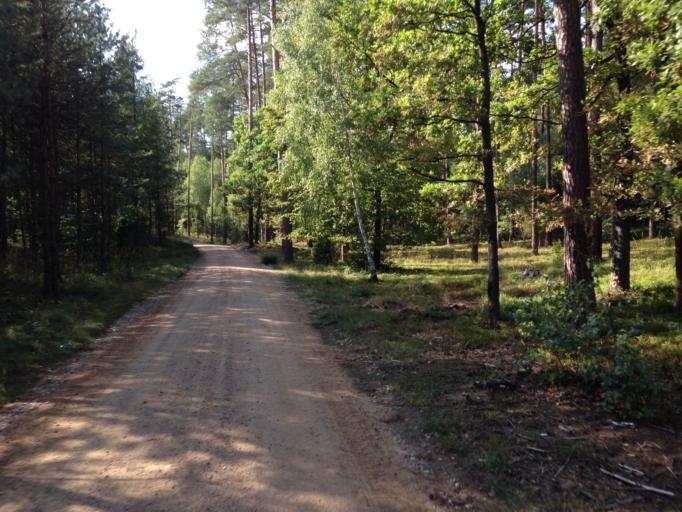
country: PL
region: Kujawsko-Pomorskie
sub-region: Powiat brodnicki
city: Gorzno
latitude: 53.1893
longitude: 19.6953
